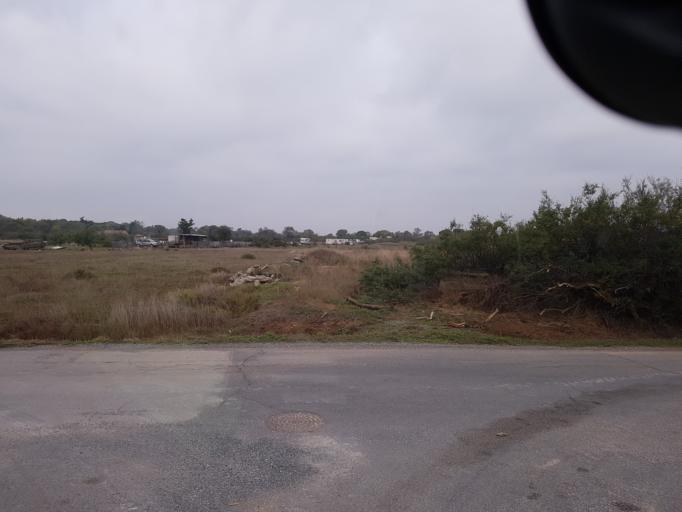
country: FR
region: Languedoc-Roussillon
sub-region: Departement de l'Herault
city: Marseillan
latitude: 43.3654
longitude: 3.5363
